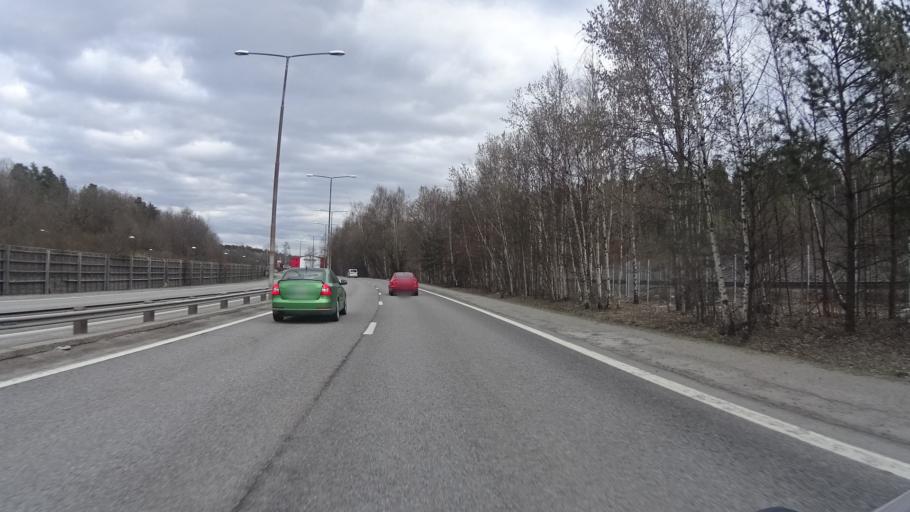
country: SE
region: Stockholm
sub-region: Stockholms Kommun
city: Arsta
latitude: 59.2643
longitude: 18.0254
